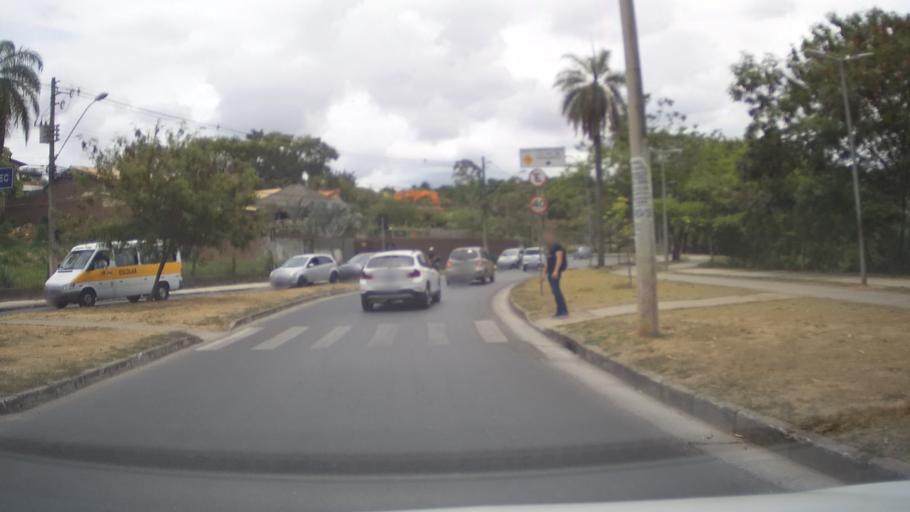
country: BR
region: Minas Gerais
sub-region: Contagem
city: Contagem
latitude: -19.8531
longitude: -44.0055
